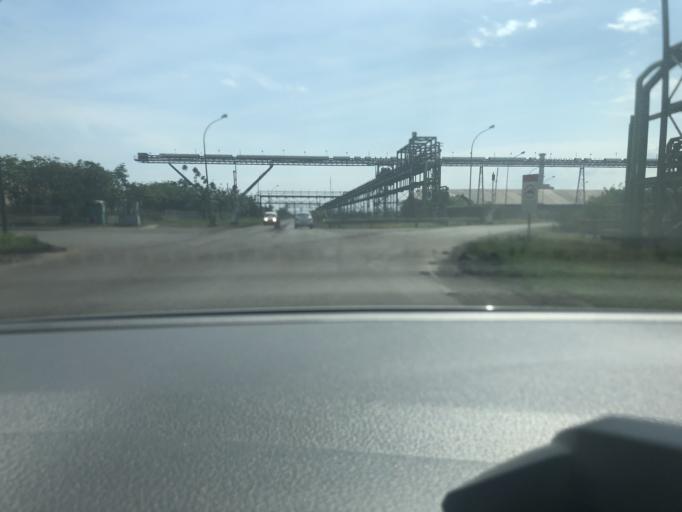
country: BR
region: Rio de Janeiro
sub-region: Itaguai
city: Itaguai
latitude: -22.9132
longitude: -43.7355
